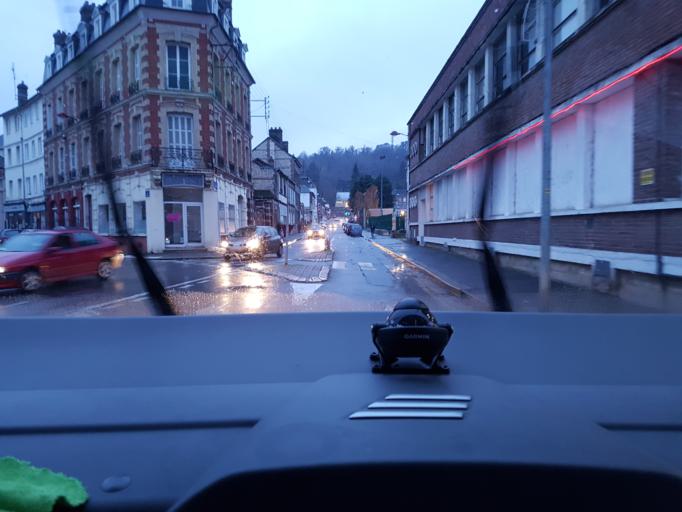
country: FR
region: Haute-Normandie
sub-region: Departement de la Seine-Maritime
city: Elbeuf
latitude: 49.2883
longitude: 1.0066
